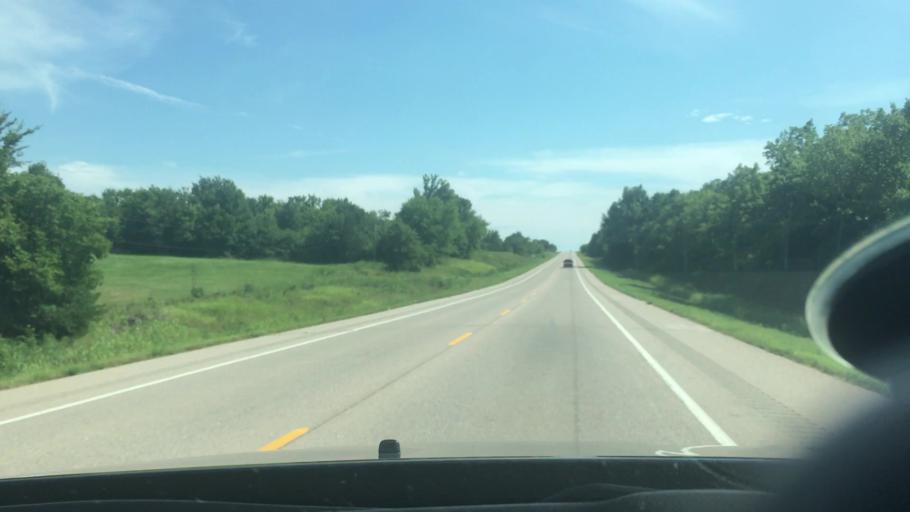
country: US
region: Oklahoma
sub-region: Seminole County
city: Konawa
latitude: 35.0087
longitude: -96.6787
